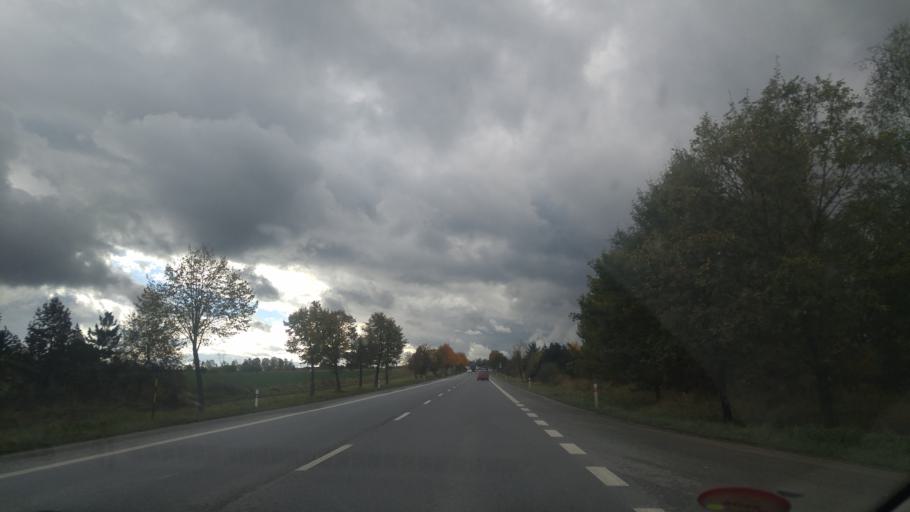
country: CZ
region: Jihocesky
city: Sevetin
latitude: 49.1180
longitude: 14.5894
